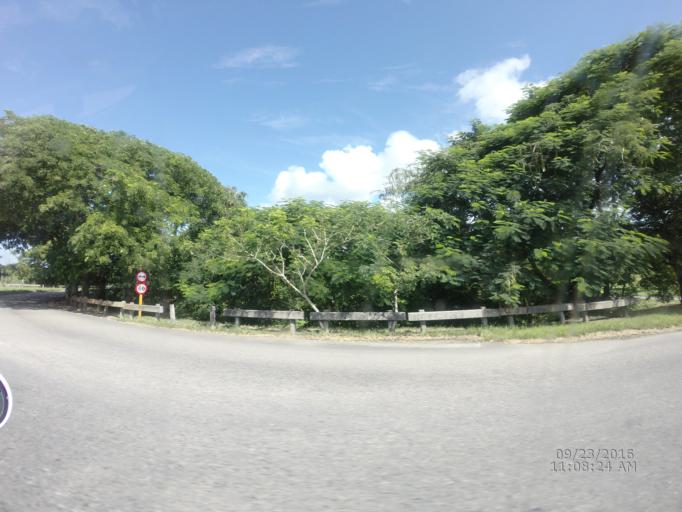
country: CU
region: Mayabeque
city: Jamaica
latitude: 23.0156
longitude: -82.2300
